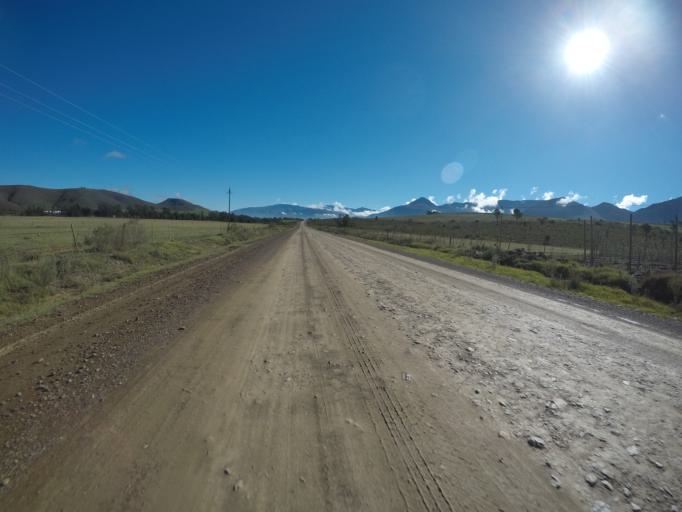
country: ZA
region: Western Cape
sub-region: Overberg District Municipality
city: Caledon
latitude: -34.0867
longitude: 19.6543
